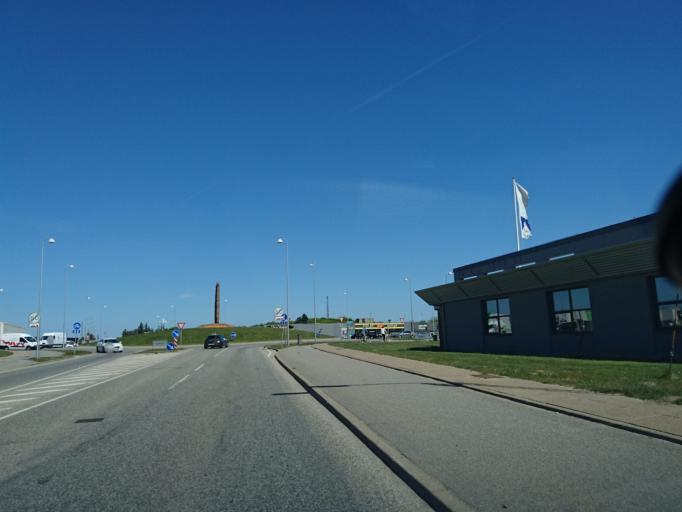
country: DK
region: North Denmark
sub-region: Hjorring Kommune
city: Hjorring
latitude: 57.4551
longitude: 10.0177
